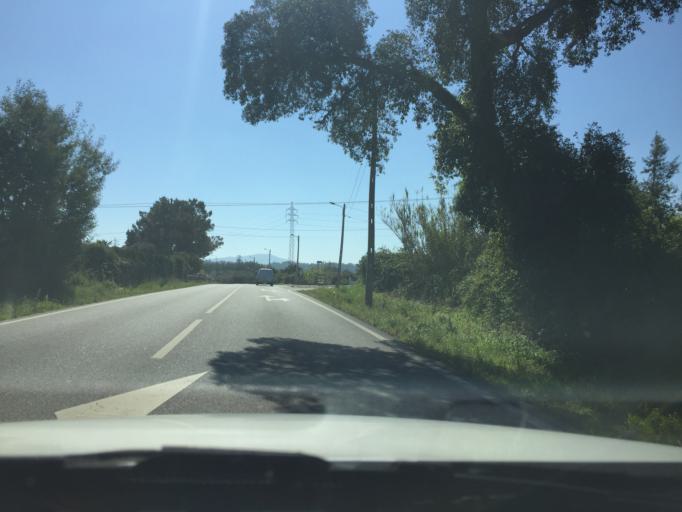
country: PT
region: Aveiro
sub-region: Anadia
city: Arcos
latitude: 40.4459
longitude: -8.4603
